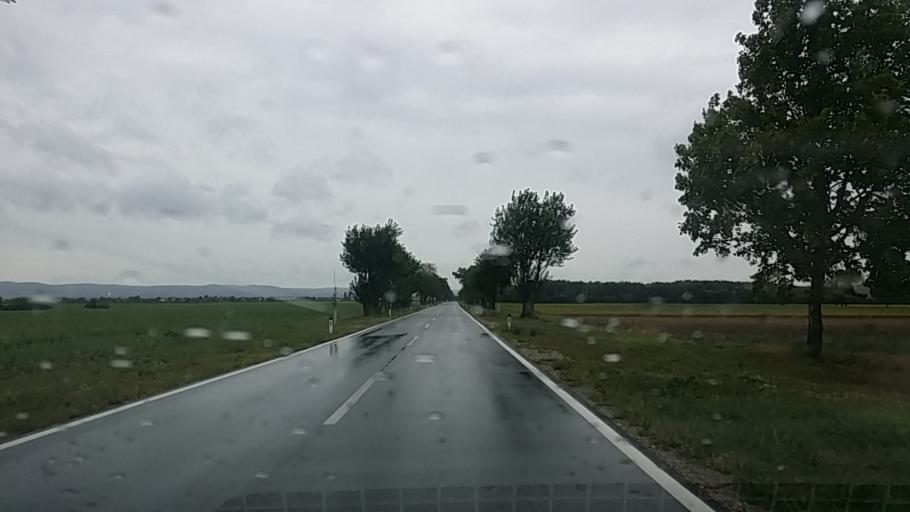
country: AT
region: Burgenland
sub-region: Eisenstadt-Umgebung
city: Sankt Margarethen im Burgenland
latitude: 47.7818
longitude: 16.6166
